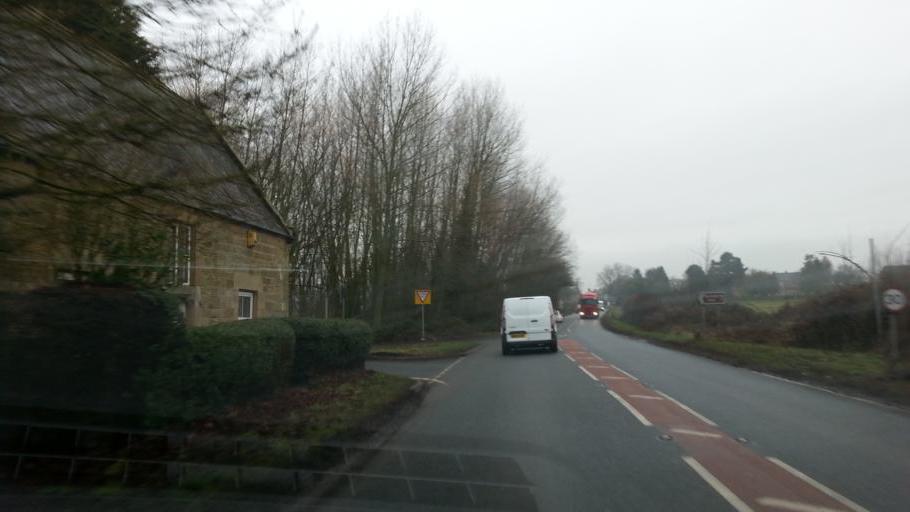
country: GB
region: England
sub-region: City and Borough of Wakefield
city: Low Ackworth
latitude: 53.6582
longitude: -1.3018
